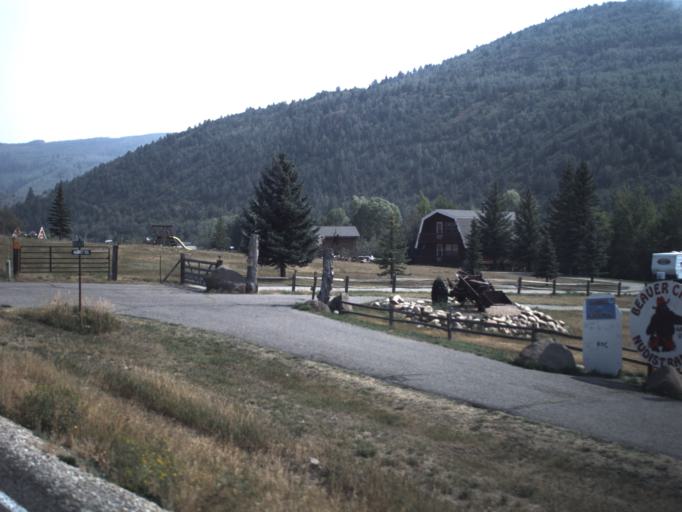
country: US
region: Utah
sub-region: Summit County
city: Francis
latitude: 40.6205
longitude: -111.2200
